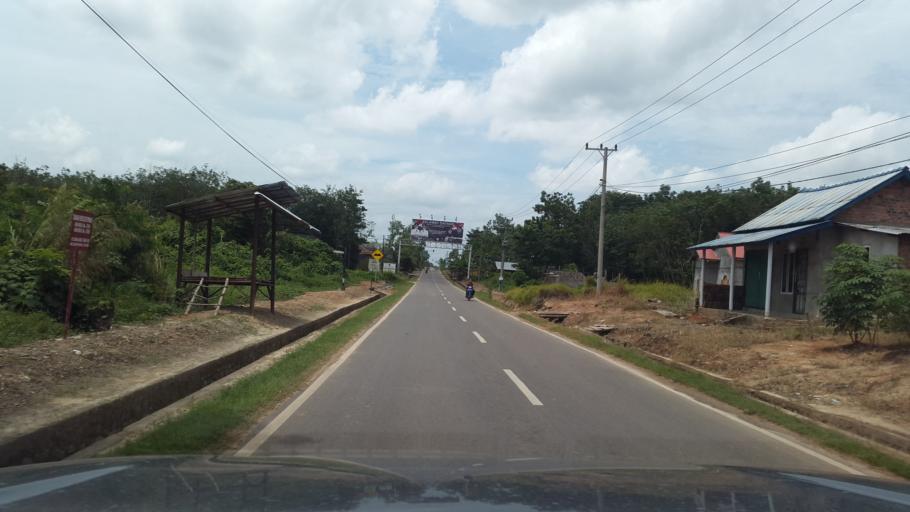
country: ID
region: South Sumatra
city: Gunungmegang Dalam
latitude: -3.3132
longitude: 103.8861
